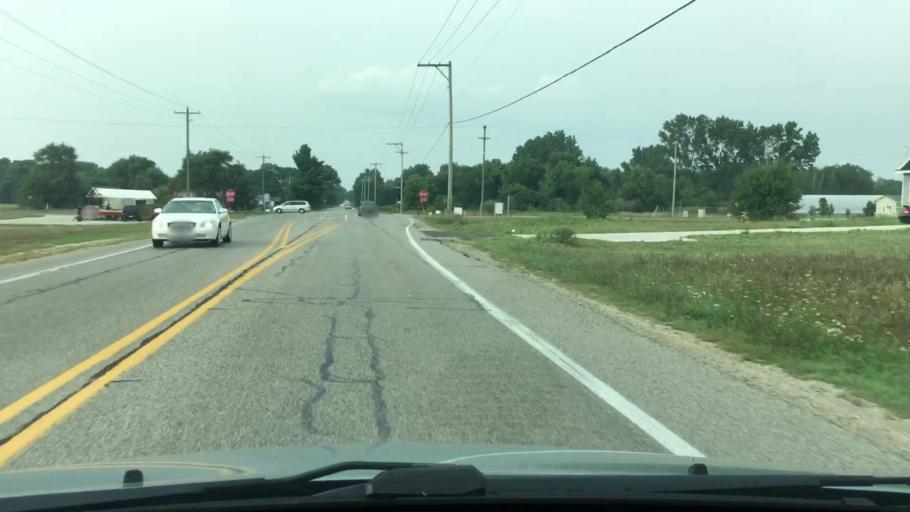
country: US
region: Michigan
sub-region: Ottawa County
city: Hudsonville
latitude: 42.9060
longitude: -85.9021
